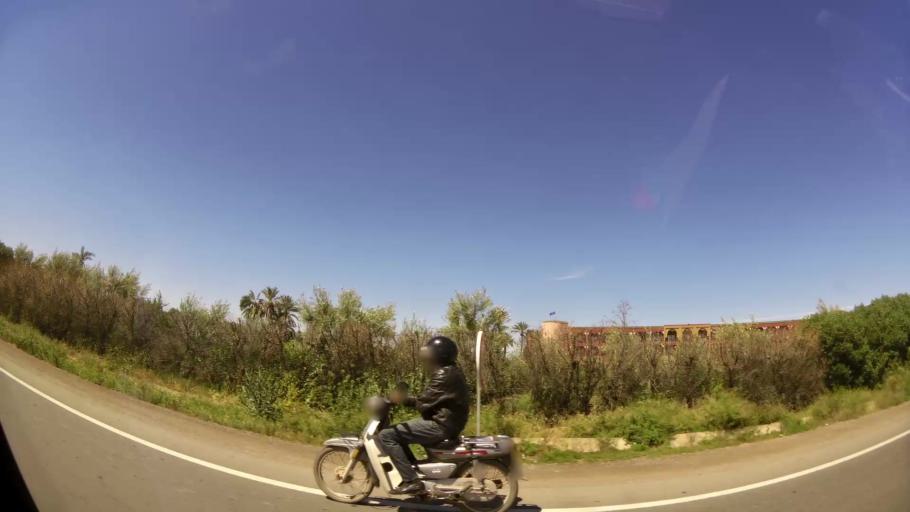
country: MA
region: Marrakech-Tensift-Al Haouz
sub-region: Marrakech
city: Marrakesh
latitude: 31.6829
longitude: -7.9917
